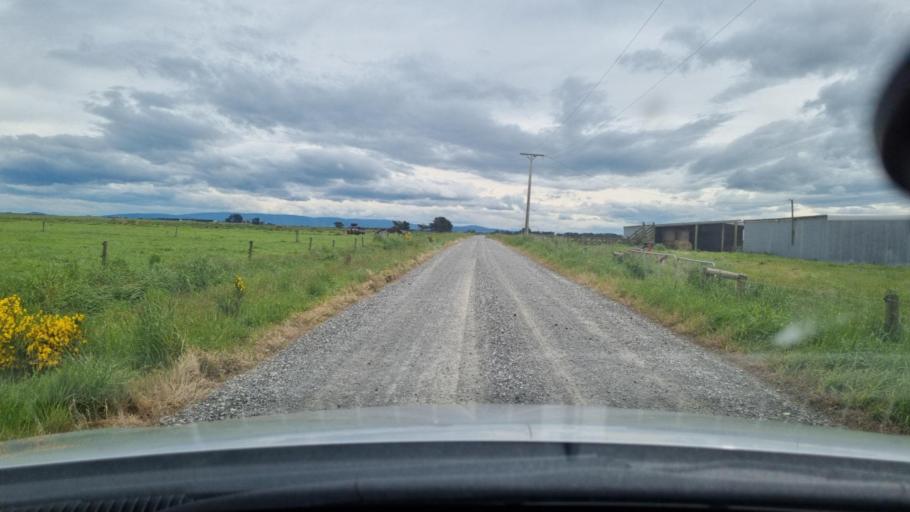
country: NZ
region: Southland
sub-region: Invercargill City
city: Invercargill
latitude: -46.4029
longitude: 168.2869
